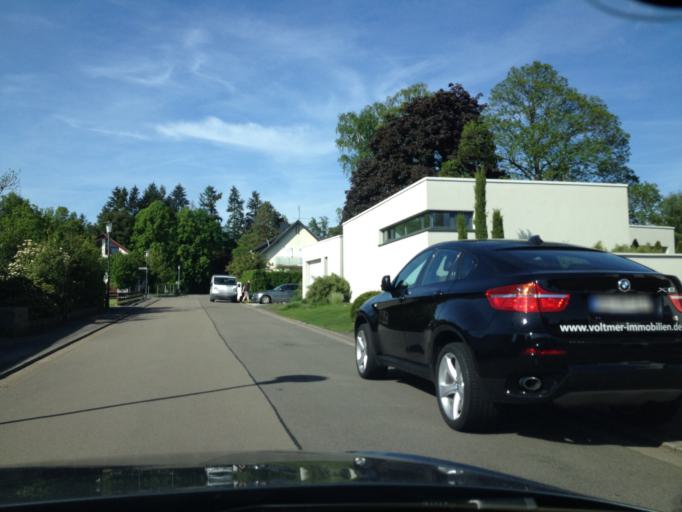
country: DE
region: Saarland
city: Bexbach
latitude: 49.3257
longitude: 7.2395
